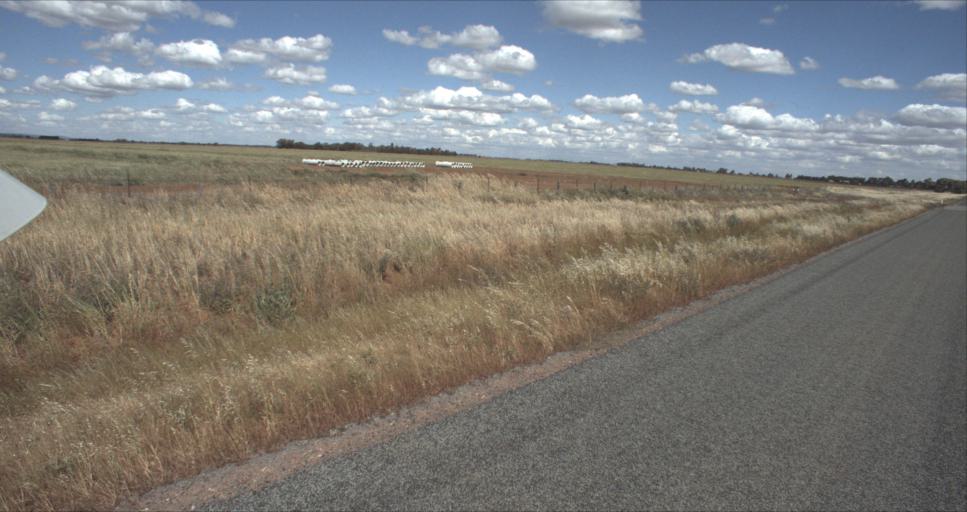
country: AU
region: New South Wales
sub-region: Leeton
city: Leeton
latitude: -34.4645
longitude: 146.2521
